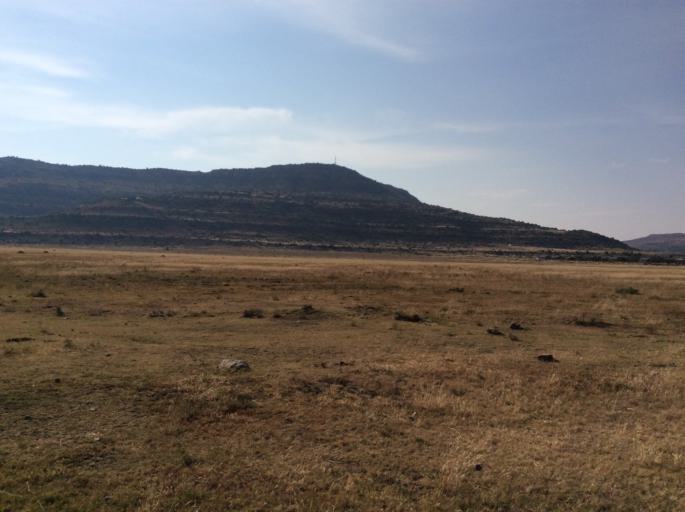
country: LS
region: Mafeteng
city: Mafeteng
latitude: -29.7076
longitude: 27.0084
